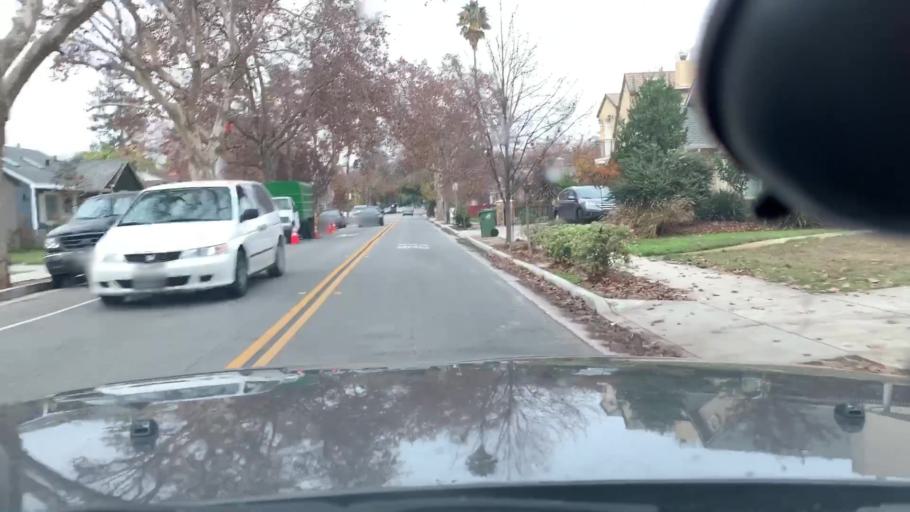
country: US
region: California
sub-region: Santa Clara County
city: Buena Vista
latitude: 37.3080
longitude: -121.8927
